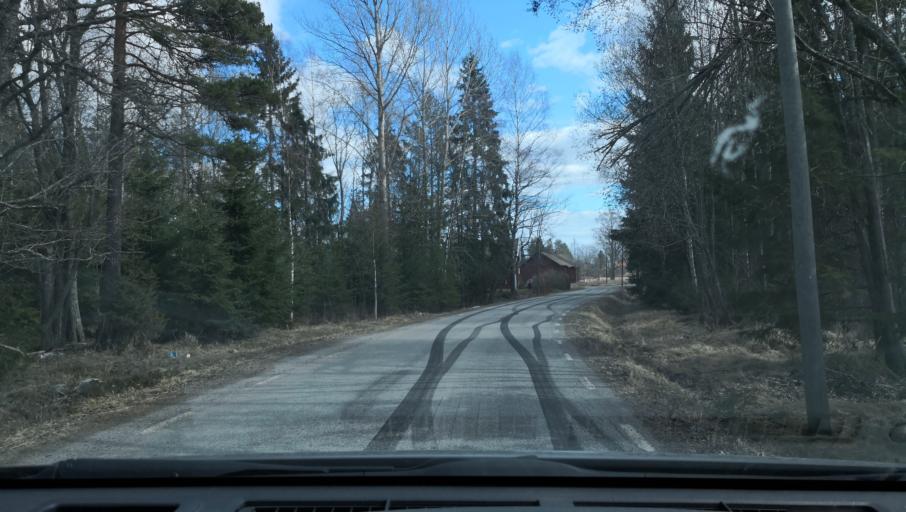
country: SE
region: Vaestmanland
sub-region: Sala Kommun
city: Sala
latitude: 59.8655
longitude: 16.5654
